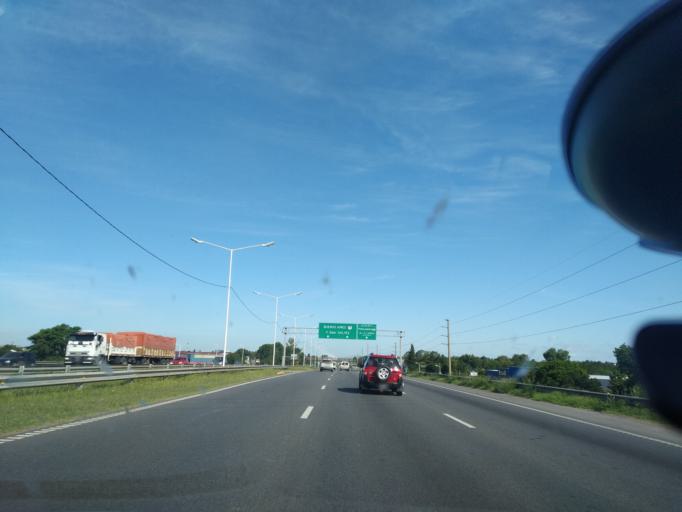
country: AR
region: Santa Fe
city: Gobernador Galvez
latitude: -33.0012
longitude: -60.6889
